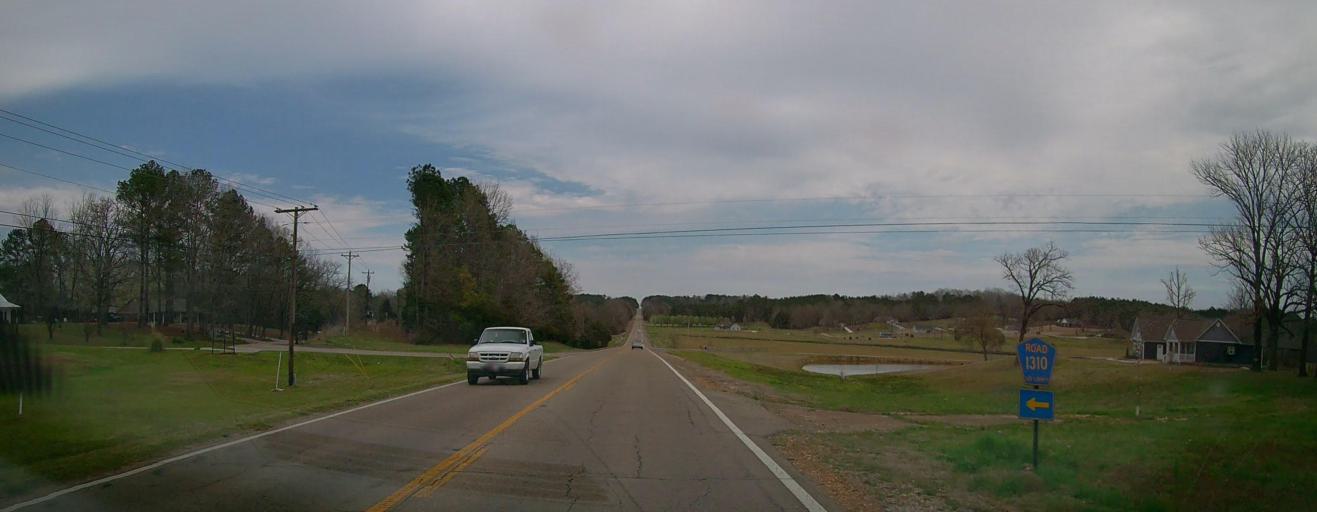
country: US
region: Mississippi
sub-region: Lee County
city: Plantersville
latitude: 34.2660
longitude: -88.6112
